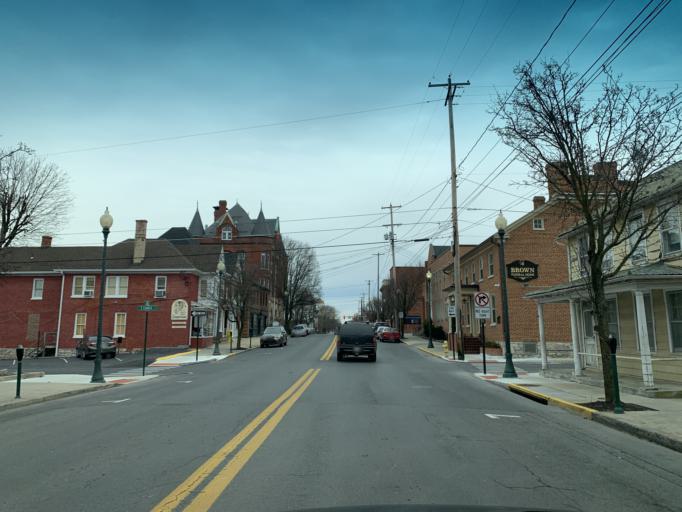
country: US
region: West Virginia
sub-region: Berkeley County
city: Martinsburg
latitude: 39.4570
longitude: -77.9680
